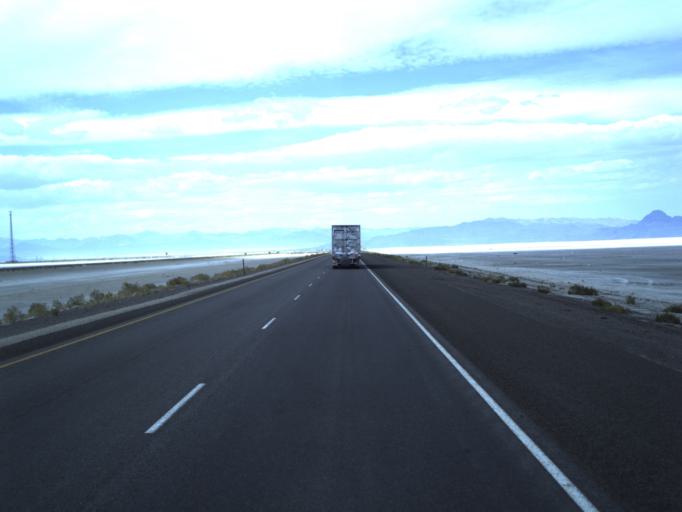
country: US
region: Utah
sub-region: Tooele County
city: Wendover
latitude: 40.7378
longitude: -113.7727
